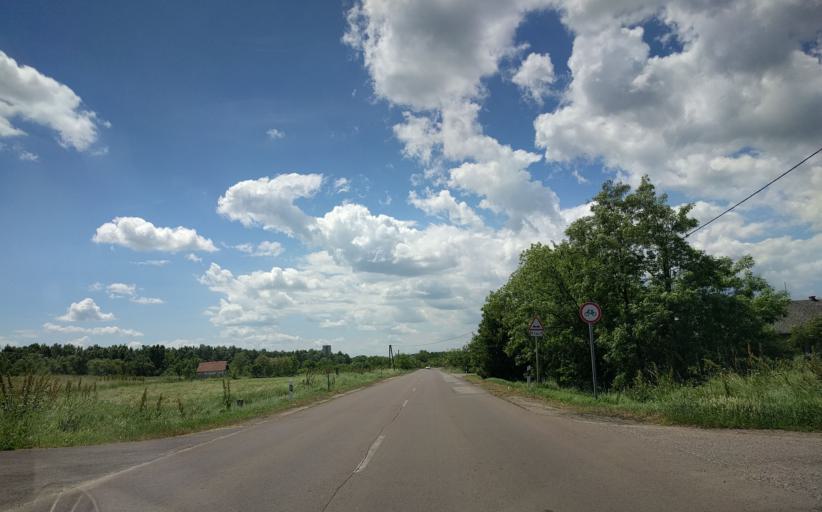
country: HU
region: Jasz-Nagykun-Szolnok
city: Toszeg
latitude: 47.1286
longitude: 20.1373
